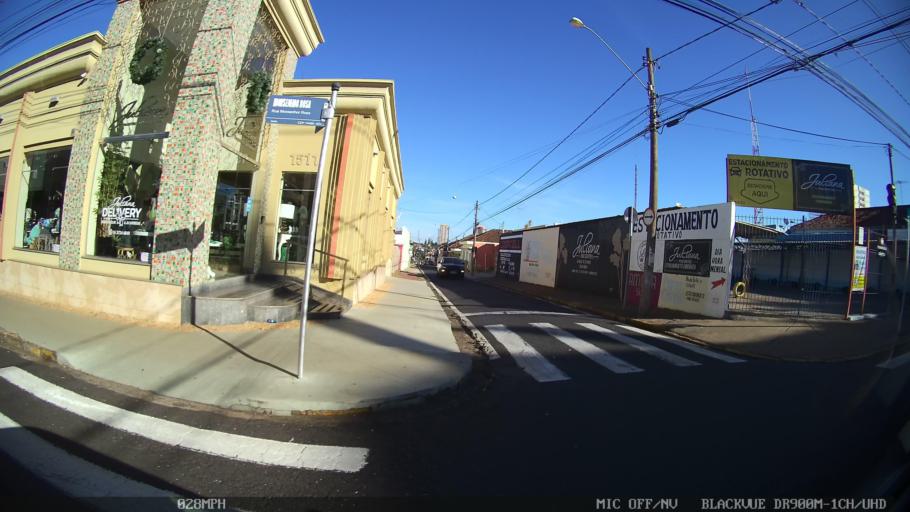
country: BR
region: Sao Paulo
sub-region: Franca
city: Franca
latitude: -20.5398
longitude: -47.4017
